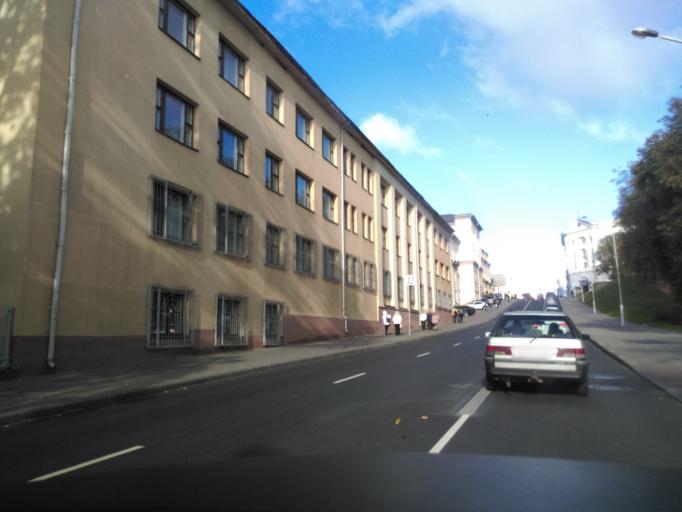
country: BY
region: Minsk
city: Minsk
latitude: 53.8966
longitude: 27.5641
